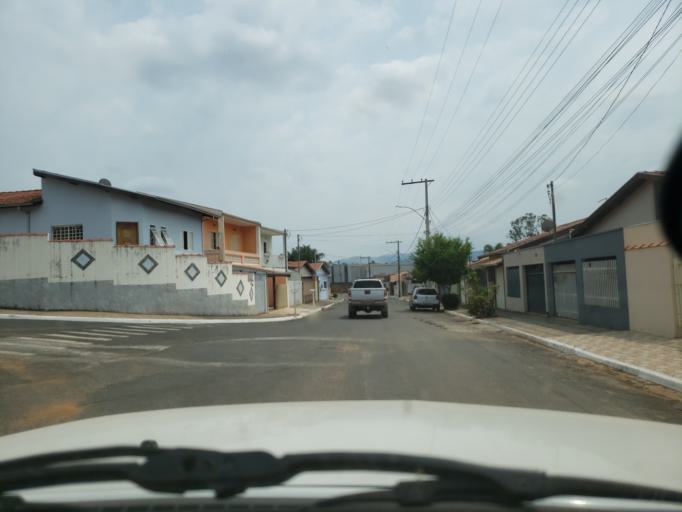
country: BR
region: Minas Gerais
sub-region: Jacutinga
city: Jacutinga
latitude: -22.3026
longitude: -46.6098
